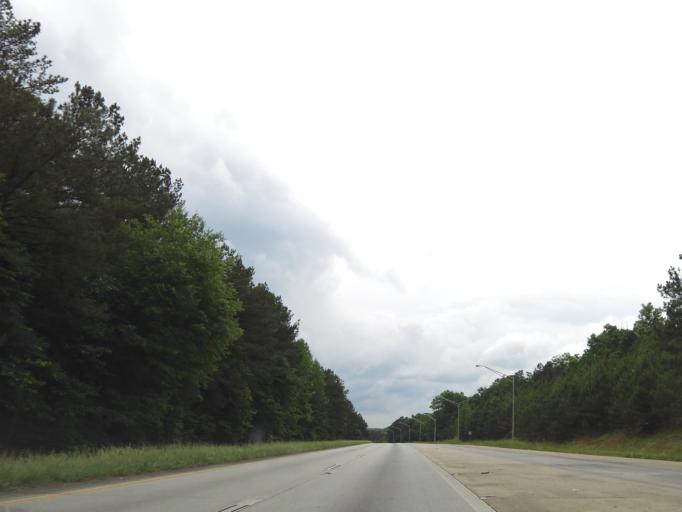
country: US
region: Georgia
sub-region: Haralson County
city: Bremen
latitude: 33.6952
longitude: -85.0890
